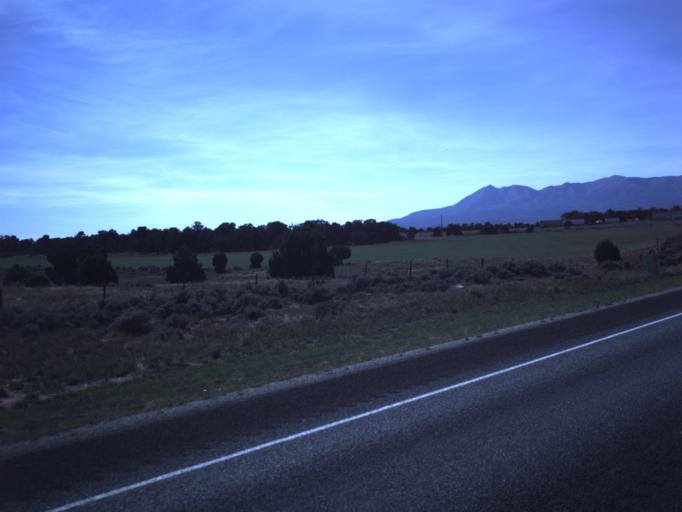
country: US
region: Utah
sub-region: San Juan County
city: Monticello
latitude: 37.8551
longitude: -109.1861
